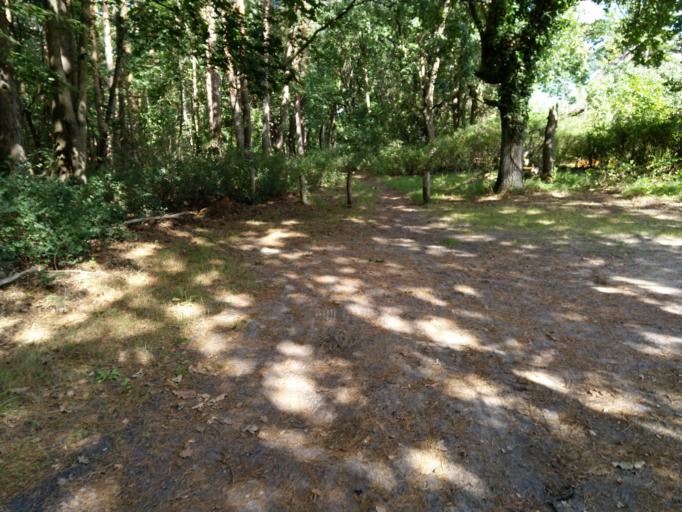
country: DE
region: Brandenburg
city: Schoneiche
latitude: 52.4556
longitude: 13.6983
